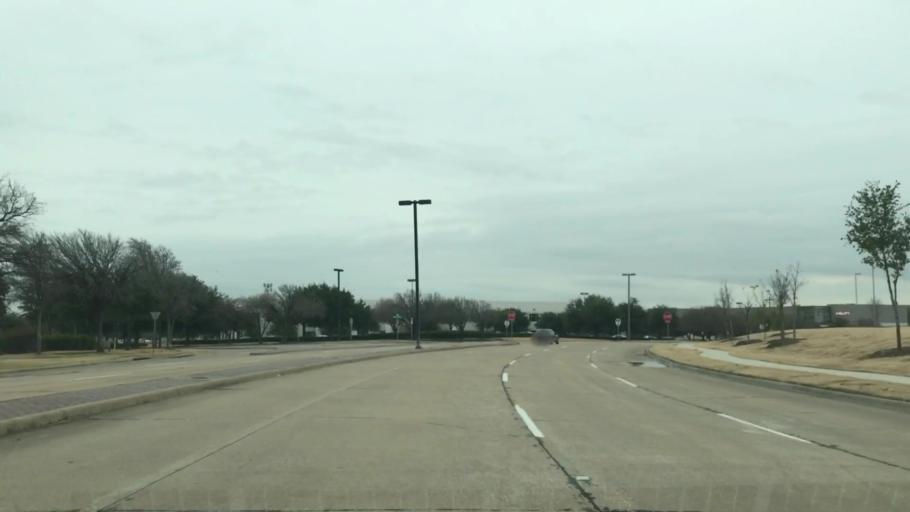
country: US
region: Texas
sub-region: Dallas County
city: Coppell
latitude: 32.9204
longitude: -97.0004
